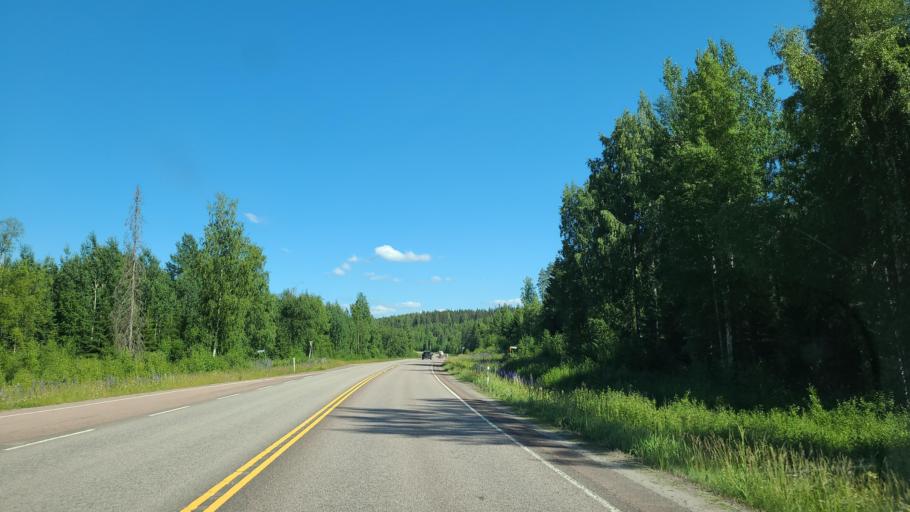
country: FI
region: Central Finland
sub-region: Jyvaeskylae
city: Petaejaevesi
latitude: 62.2733
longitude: 25.3632
